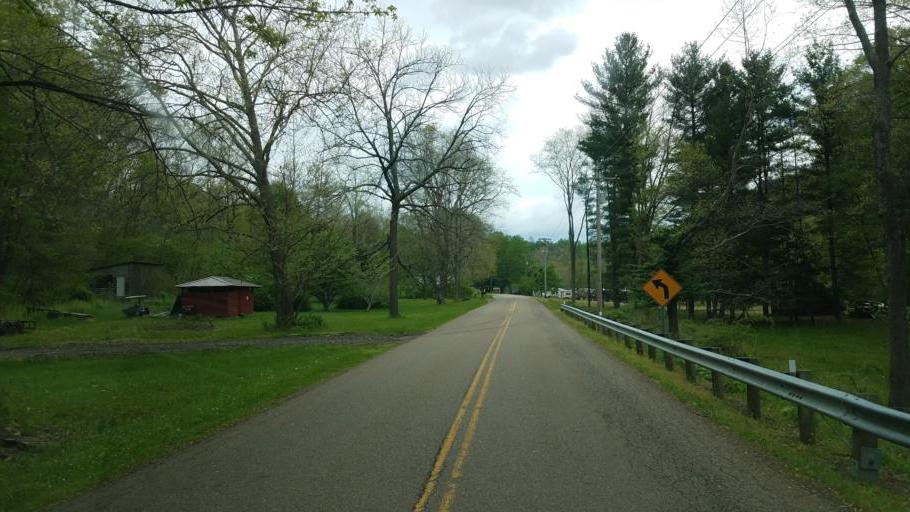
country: US
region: Ohio
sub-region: Ashland County
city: Loudonville
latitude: 40.5873
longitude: -82.1905
